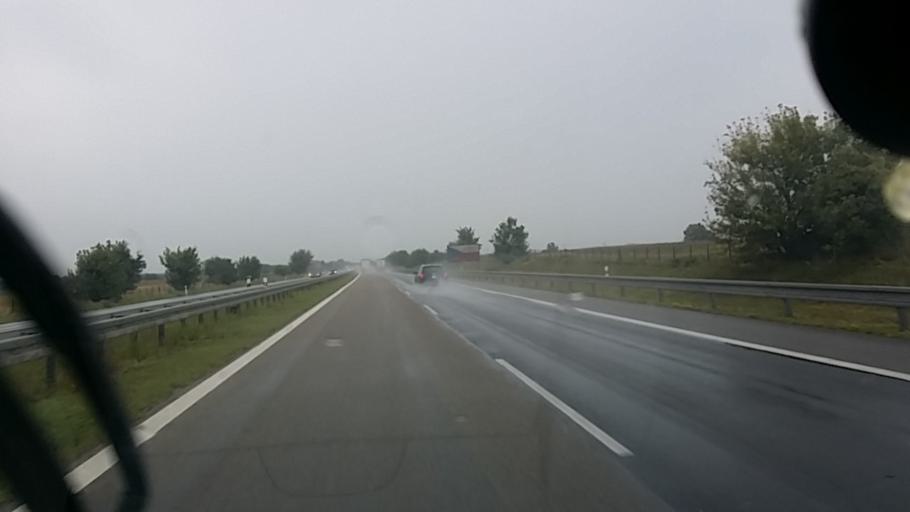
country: CZ
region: South Moravian
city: Kostice
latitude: 48.7568
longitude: 16.9518
